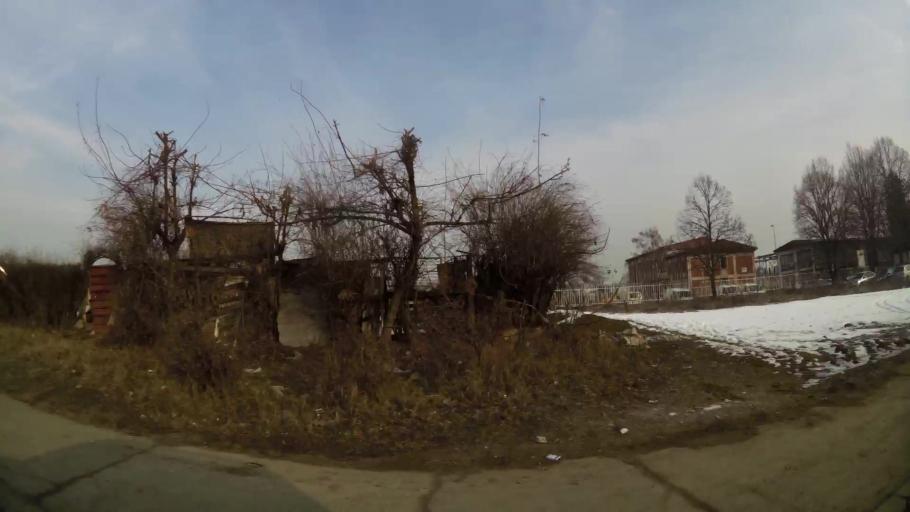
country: MK
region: Butel
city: Butel
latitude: 42.0250
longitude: 21.4425
